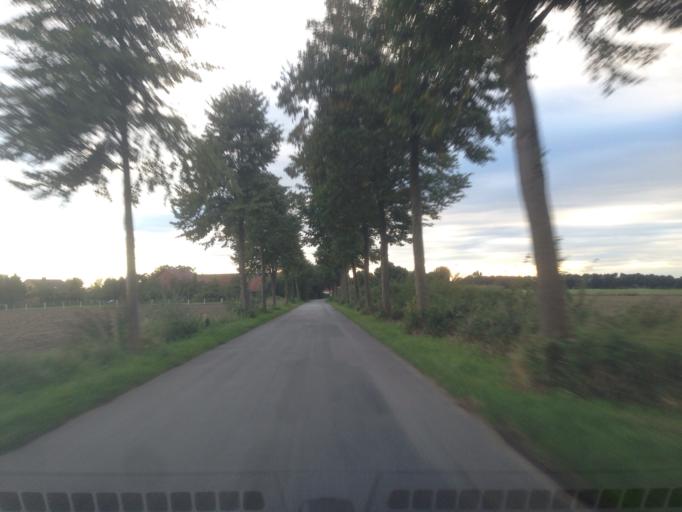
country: DE
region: North Rhine-Westphalia
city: Olfen
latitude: 51.7436
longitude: 7.3855
